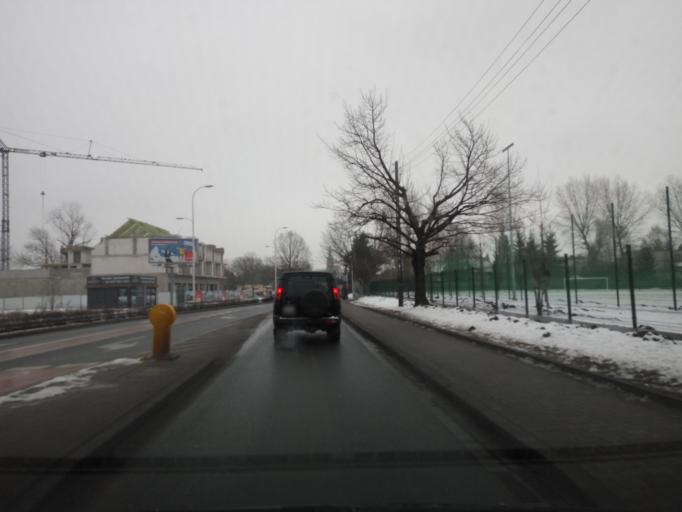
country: PL
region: Lower Silesian Voivodeship
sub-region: Powiat wroclawski
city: Wroclaw
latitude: 51.0584
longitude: 17.0146
